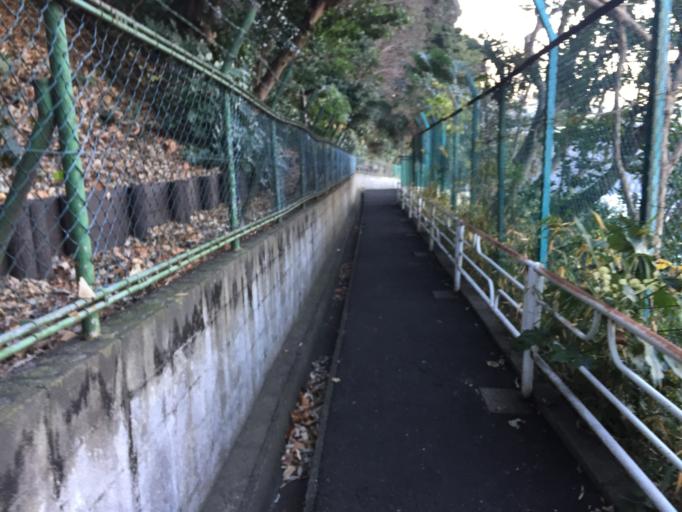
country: JP
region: Kanagawa
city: Yokohama
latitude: 35.4411
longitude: 139.6541
